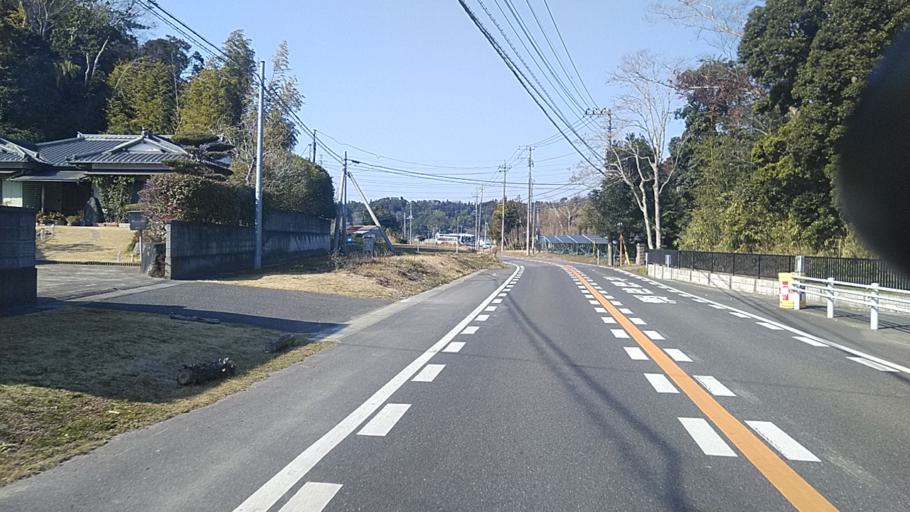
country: JP
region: Chiba
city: Mobara
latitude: 35.4615
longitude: 140.2843
